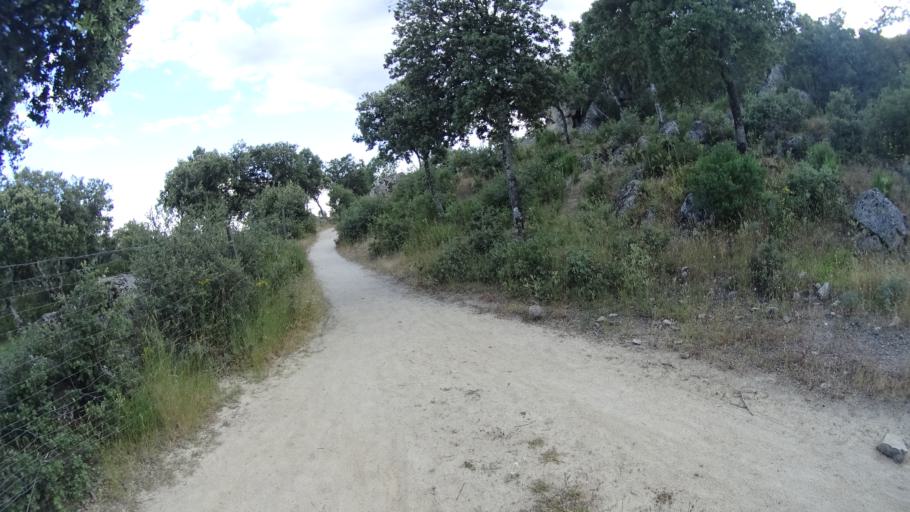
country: ES
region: Madrid
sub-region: Provincia de Madrid
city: Hoyo de Manzanares
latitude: 40.6329
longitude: -3.9100
